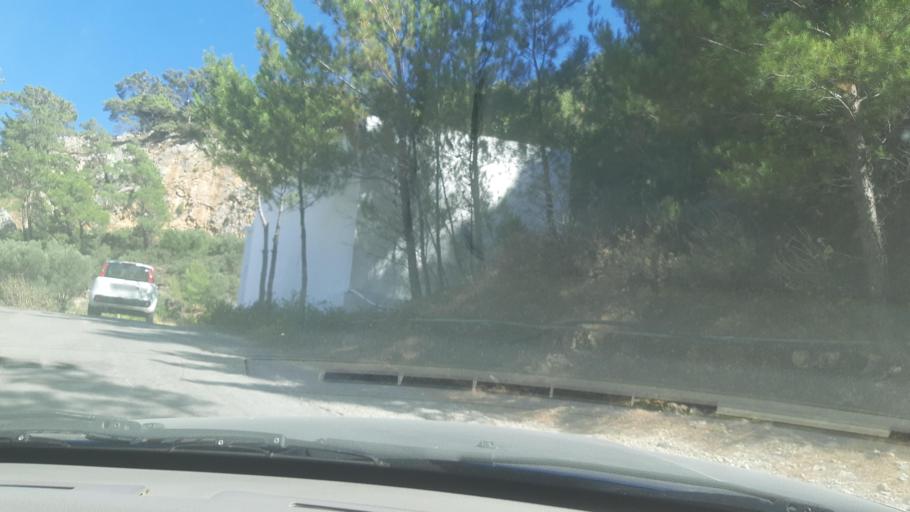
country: GR
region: South Aegean
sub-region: Nomos Dodekanisou
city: Karpathos
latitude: 35.5849
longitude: 27.1757
